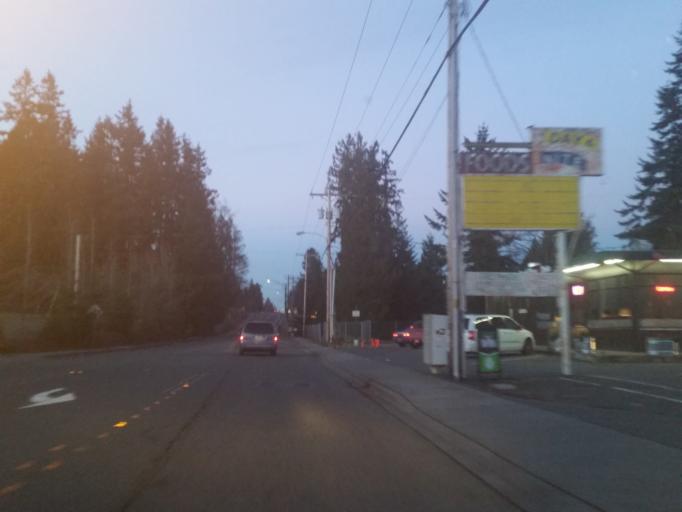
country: US
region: Washington
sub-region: Snohomish County
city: Lynnwood
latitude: 47.8473
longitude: -122.3036
